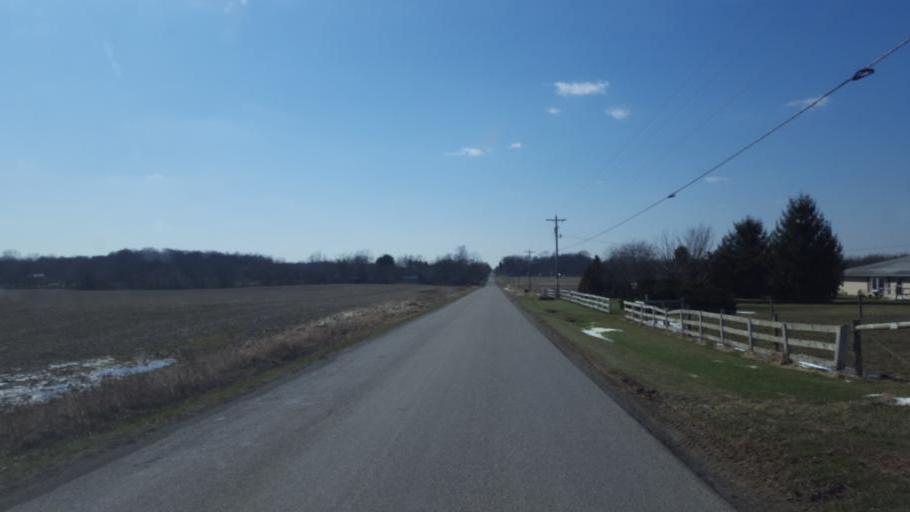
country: US
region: Ohio
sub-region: Morrow County
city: Mount Gilead
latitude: 40.4592
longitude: -82.7403
